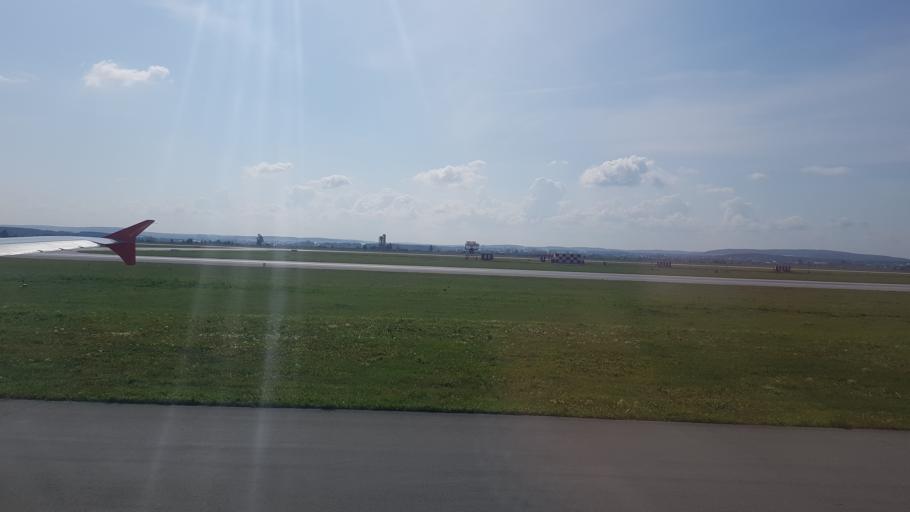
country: RU
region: Sverdlovsk
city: Istok
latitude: 56.7463
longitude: 60.8037
